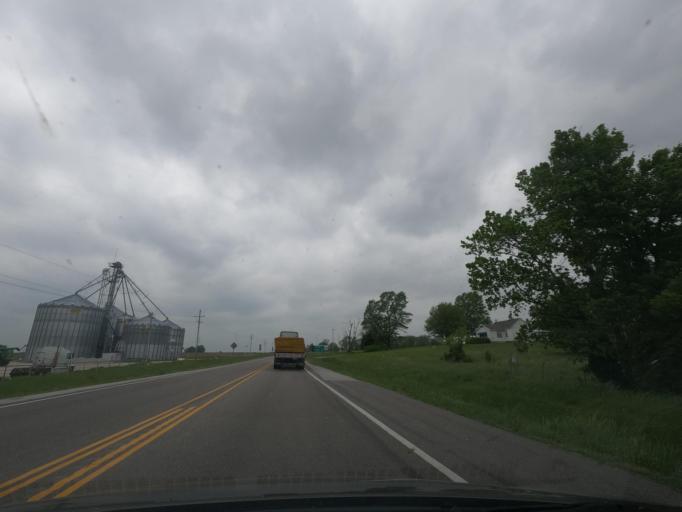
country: US
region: Kansas
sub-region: Cherokee County
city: Galena
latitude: 37.1780
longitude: -94.7070
